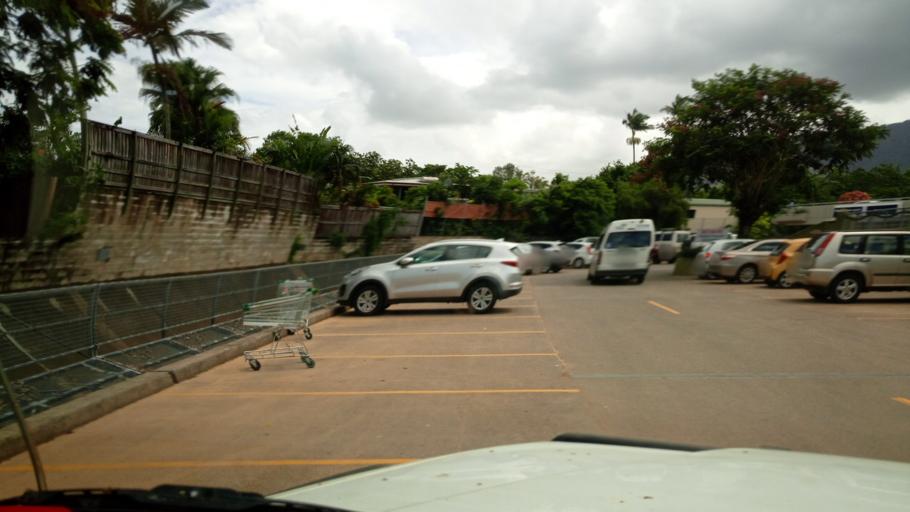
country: AU
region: Queensland
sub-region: Cairns
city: Woree
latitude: -16.9454
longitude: 145.7404
